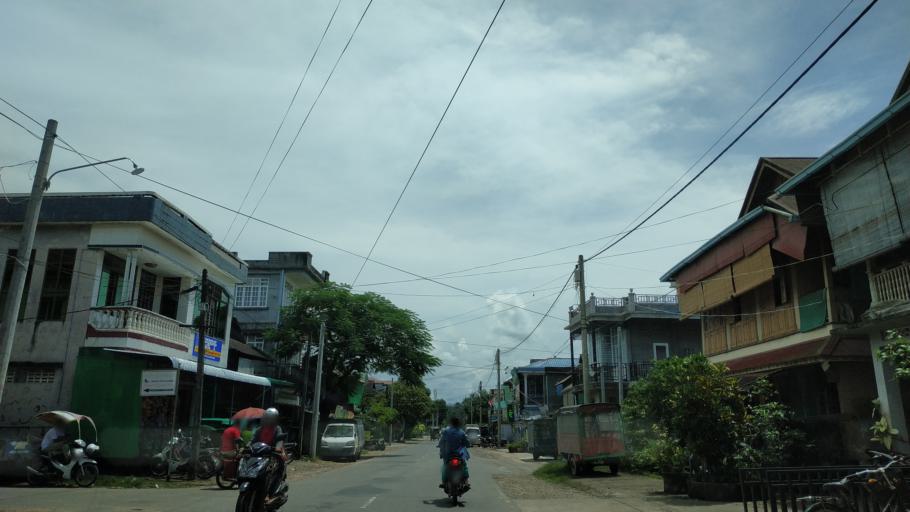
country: MM
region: Tanintharyi
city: Dawei
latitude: 14.0694
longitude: 98.1925
